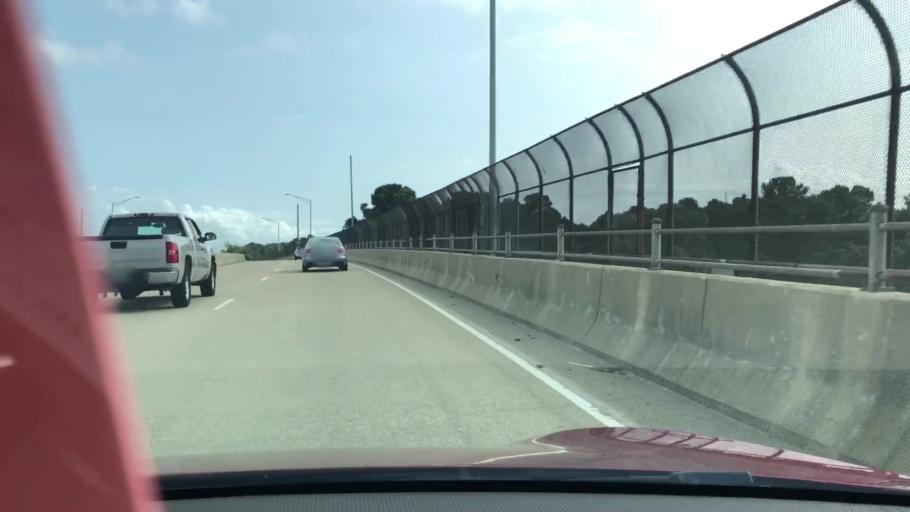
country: US
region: Virginia
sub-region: City of Virginia Beach
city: Virginia Beach
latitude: 36.9046
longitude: -76.0674
